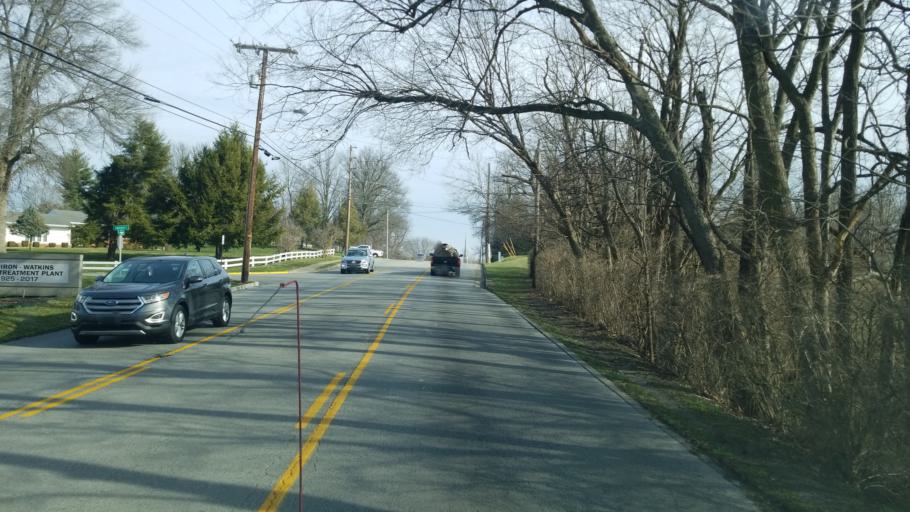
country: US
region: Kentucky
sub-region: Boyle County
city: Danville
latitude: 37.6507
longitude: -84.7611
